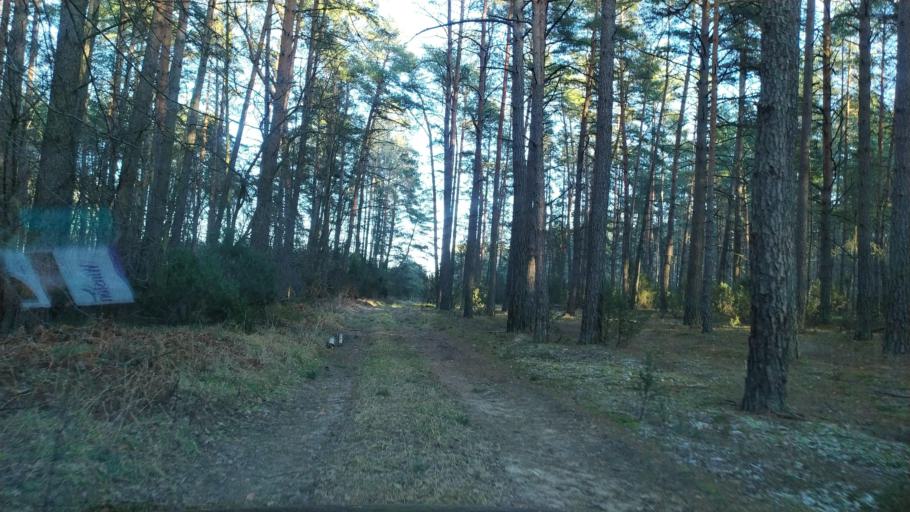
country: BY
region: Brest
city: Pruzhany
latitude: 52.5508
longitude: 24.2801
